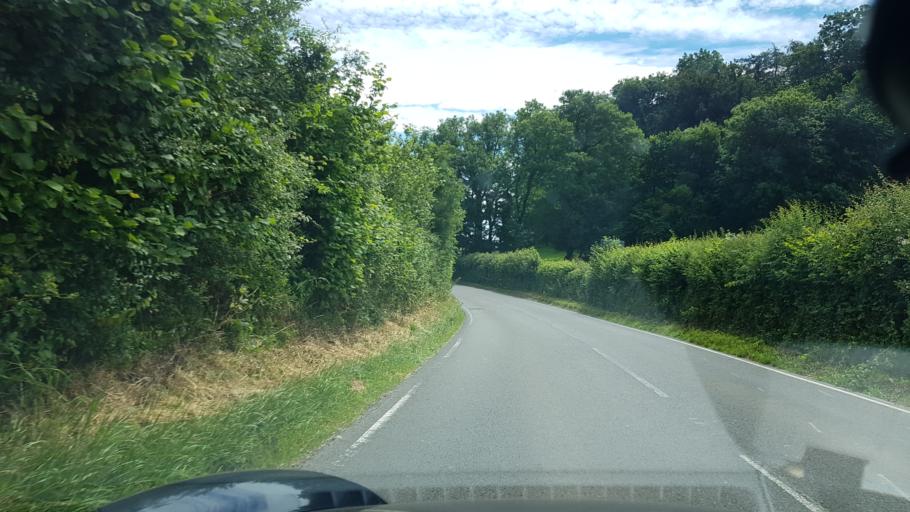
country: GB
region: Wales
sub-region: Carmarthenshire
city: Saint Clears
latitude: 51.8007
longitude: -4.4916
